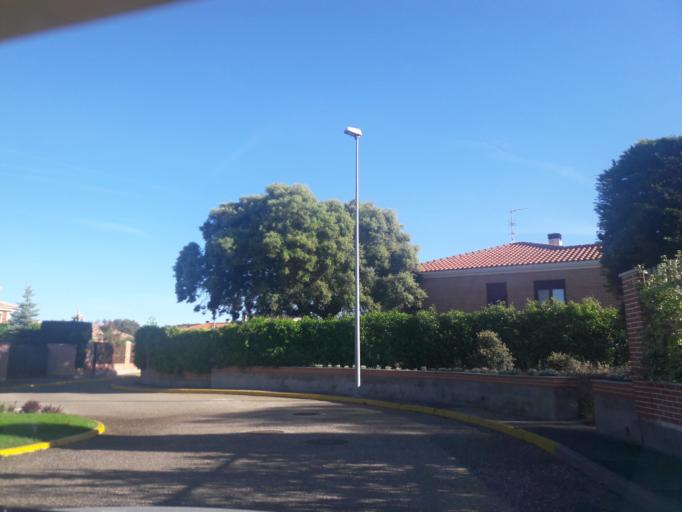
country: ES
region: Castille and Leon
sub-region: Provincia de Salamanca
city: Martinamor
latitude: 40.8070
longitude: -5.6368
